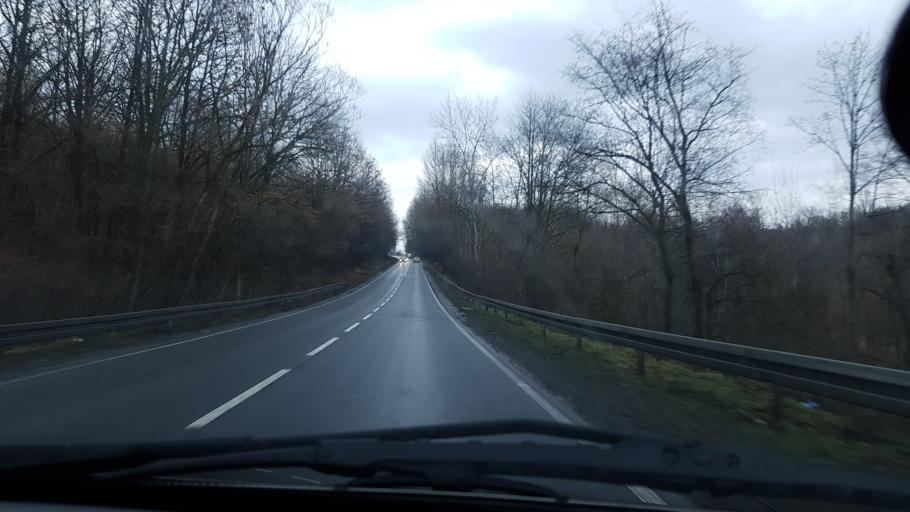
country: PL
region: Silesian Voivodeship
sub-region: Powiat zywiecki
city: Zywiec
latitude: 49.7110
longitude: 19.2185
